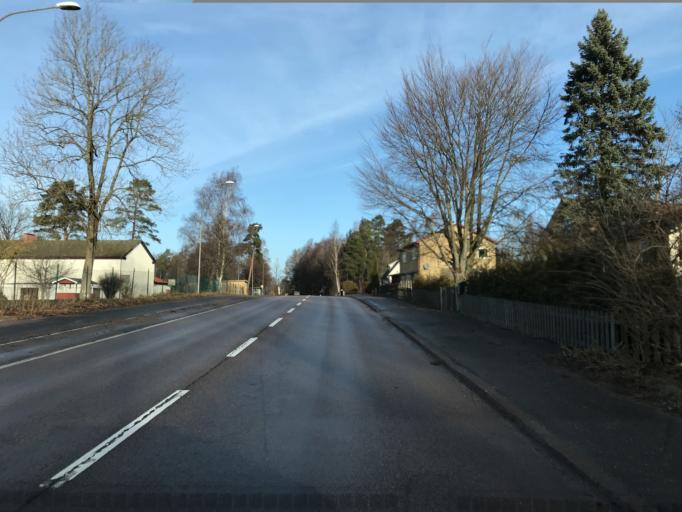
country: SE
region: Skane
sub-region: Hassleholms Kommun
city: Bjarnum
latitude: 56.2960
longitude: 13.7075
